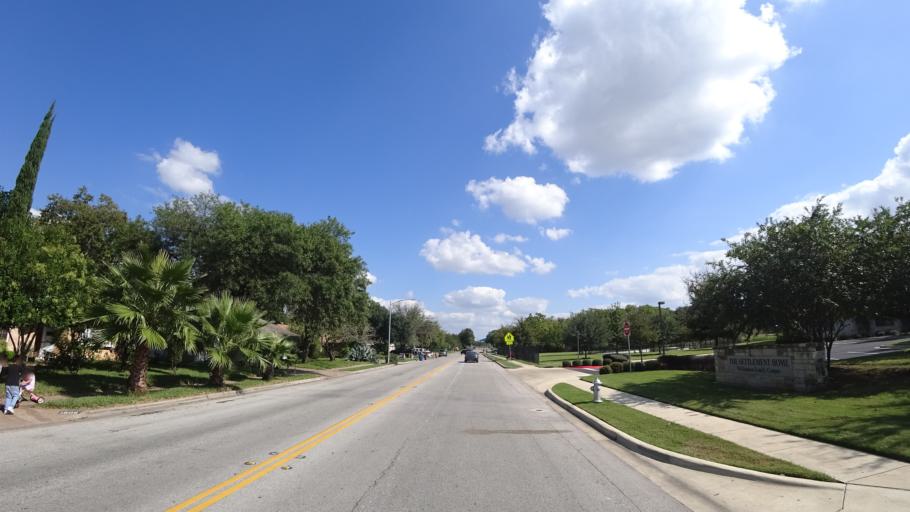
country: US
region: Texas
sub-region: Travis County
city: Wells Branch
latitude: 30.3671
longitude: -97.7127
